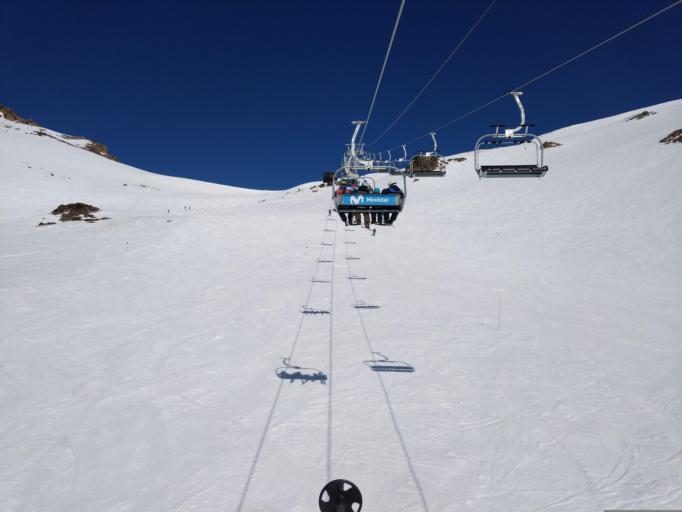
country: AR
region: Rio Negro
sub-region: Departamento de Bariloche
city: San Carlos de Bariloche
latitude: -41.1721
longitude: -71.4818
